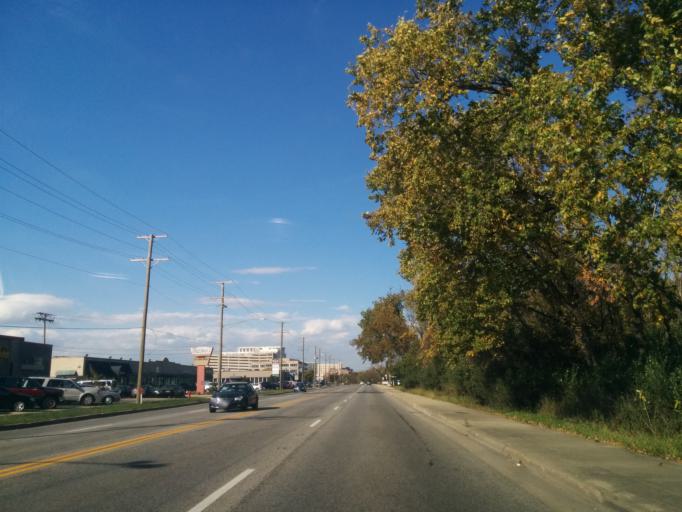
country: US
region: Illinois
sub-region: Cook County
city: Schiller Park
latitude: 41.9682
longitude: -87.8616
